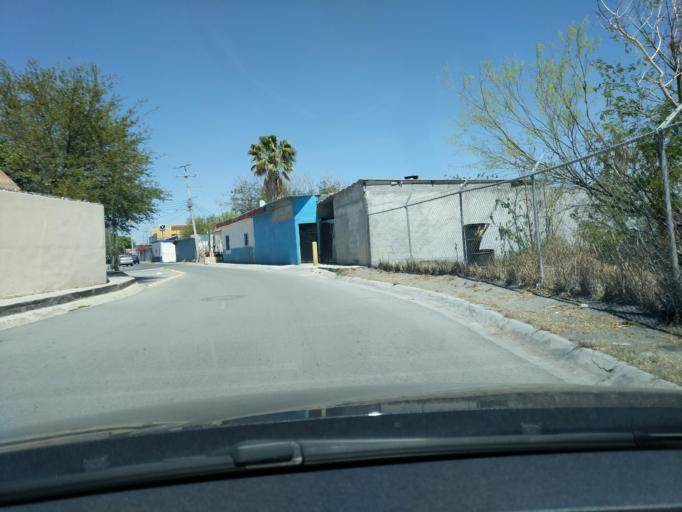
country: MX
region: Nuevo Leon
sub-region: Apodaca
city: Artemio Trevino
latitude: 25.8146
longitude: -100.1515
